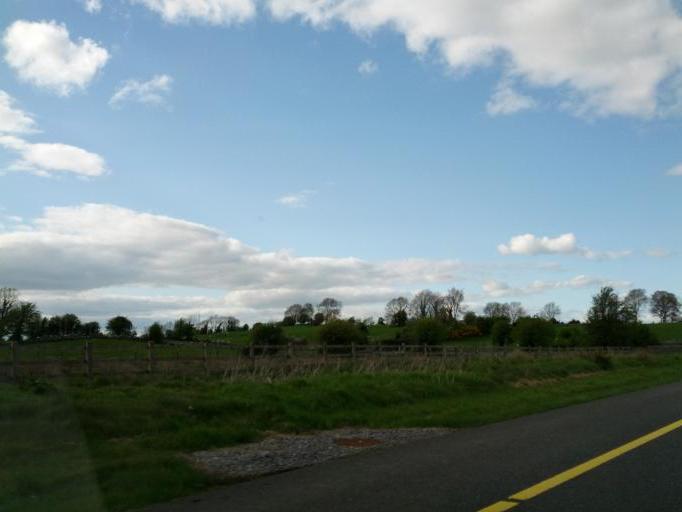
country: IE
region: Leinster
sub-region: An Iarmhi
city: Athlone
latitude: 53.3783
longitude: -8.0518
